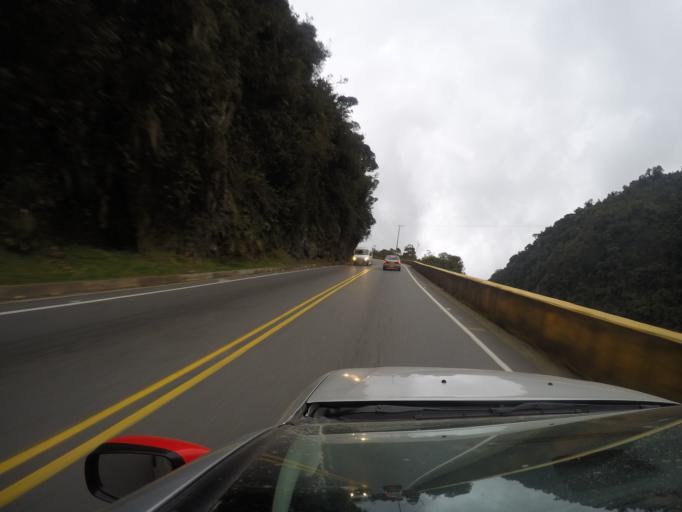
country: CO
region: Tolima
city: Herveo
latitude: 5.0803
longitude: -75.2809
